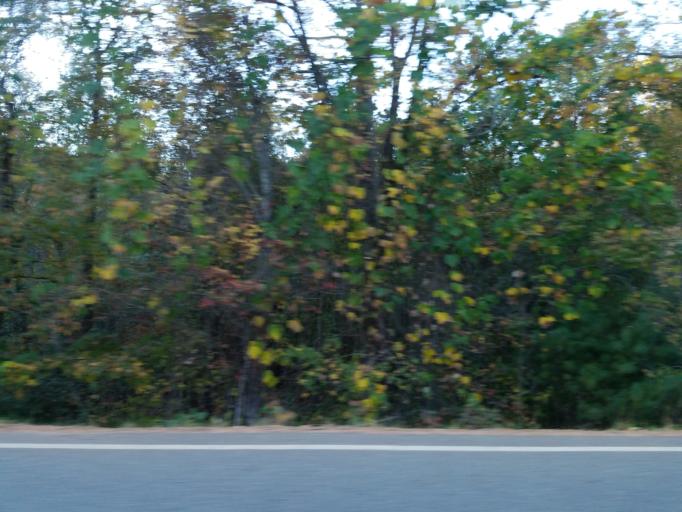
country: US
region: Georgia
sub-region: Dawson County
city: Dawsonville
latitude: 34.5526
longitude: -84.2562
